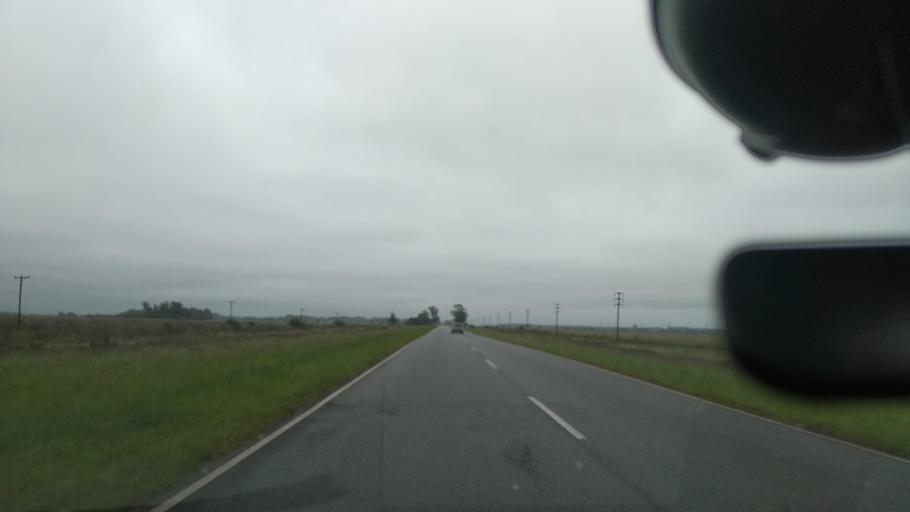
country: AR
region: Buenos Aires
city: Veronica
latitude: -35.3415
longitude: -57.4493
